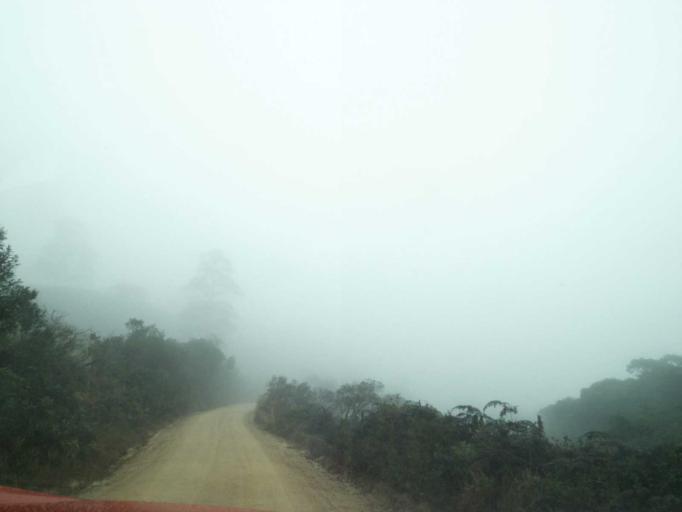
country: BR
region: Santa Catarina
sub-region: Anitapolis
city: Anitapolis
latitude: -27.9107
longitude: -49.1697
